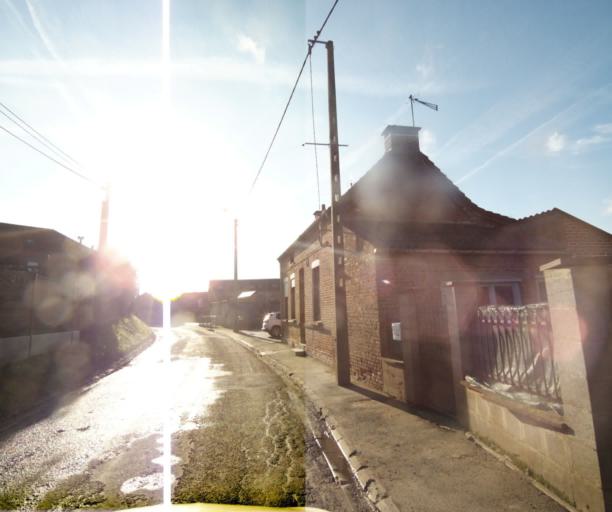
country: FR
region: Nord-Pas-de-Calais
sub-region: Departement du Nord
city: Preseau
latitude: 50.3153
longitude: 3.5747
